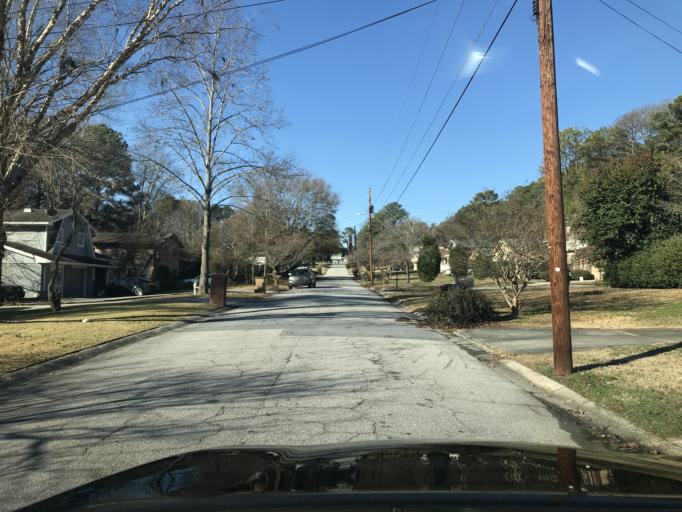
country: US
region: Georgia
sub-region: Clayton County
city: Morrow
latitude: 33.5665
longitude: -84.3651
